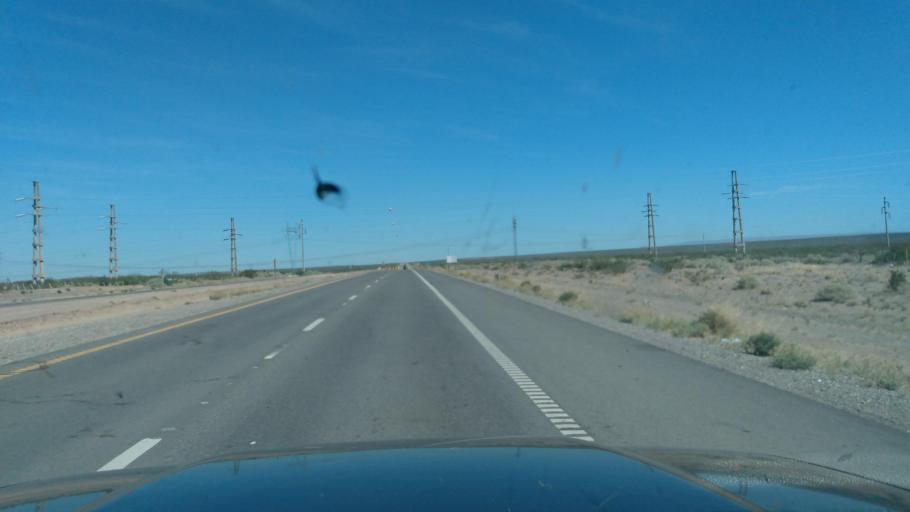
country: AR
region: Neuquen
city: Senillosa
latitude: -39.0758
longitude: -68.5941
